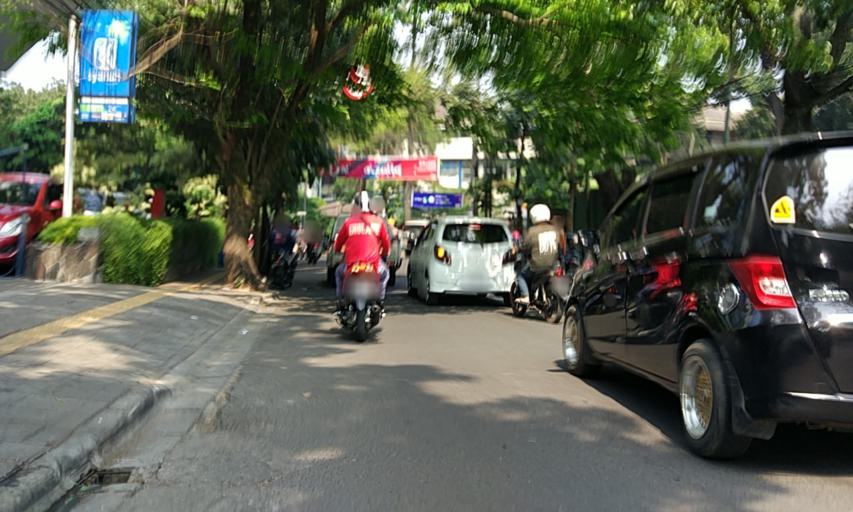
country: ID
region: West Java
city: Bandung
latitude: -6.9029
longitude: 107.6088
